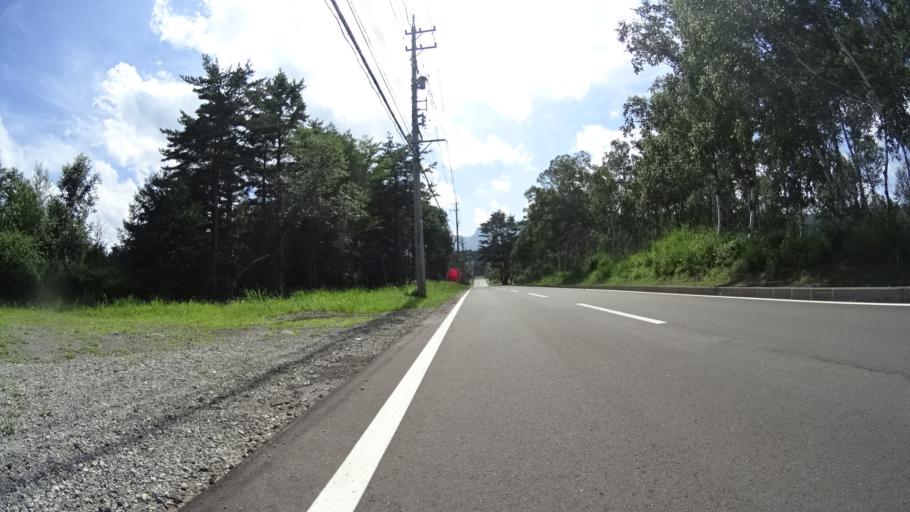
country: JP
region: Nagano
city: Saku
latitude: 36.0522
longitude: 138.4208
